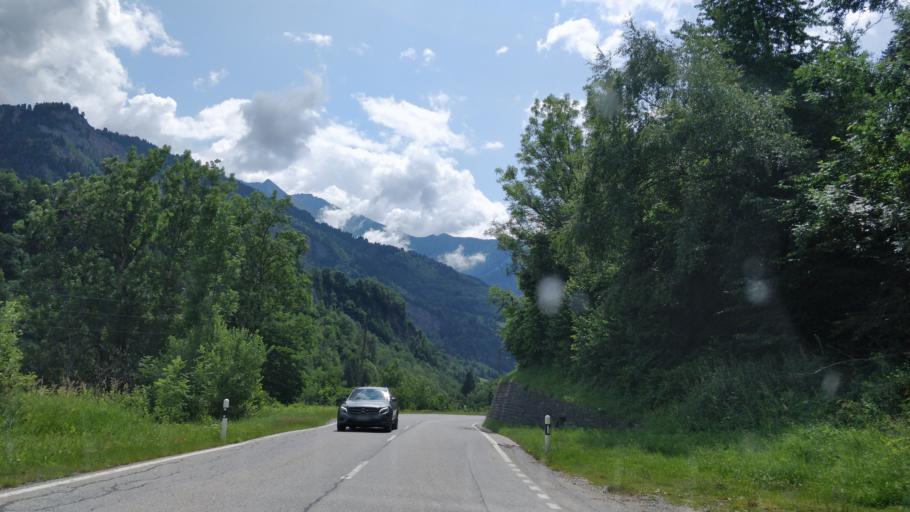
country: CH
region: Grisons
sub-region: Surselva District
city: Ilanz
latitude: 46.7650
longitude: 9.2058
